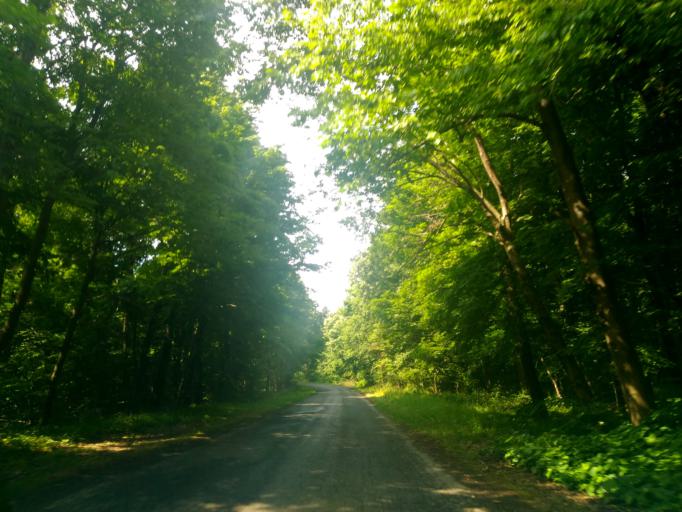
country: HU
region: Baranya
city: Pecs
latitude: 46.1214
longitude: 18.2116
